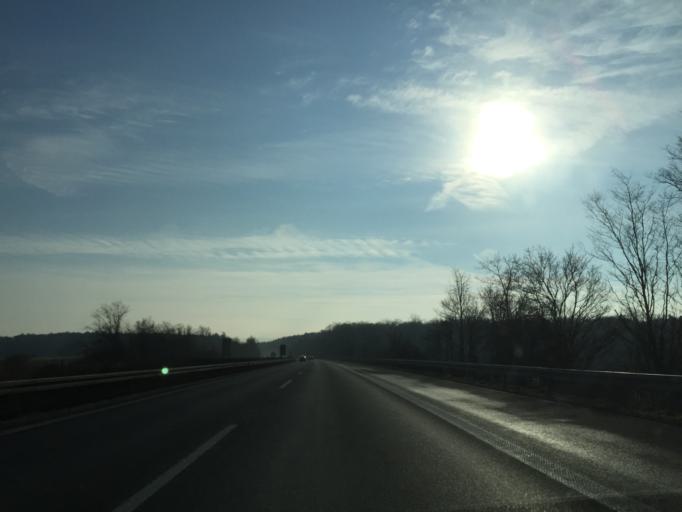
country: DE
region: Bavaria
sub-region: Regierungsbezirk Unterfranken
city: Kleinlangheim
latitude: 49.7777
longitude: 10.3036
